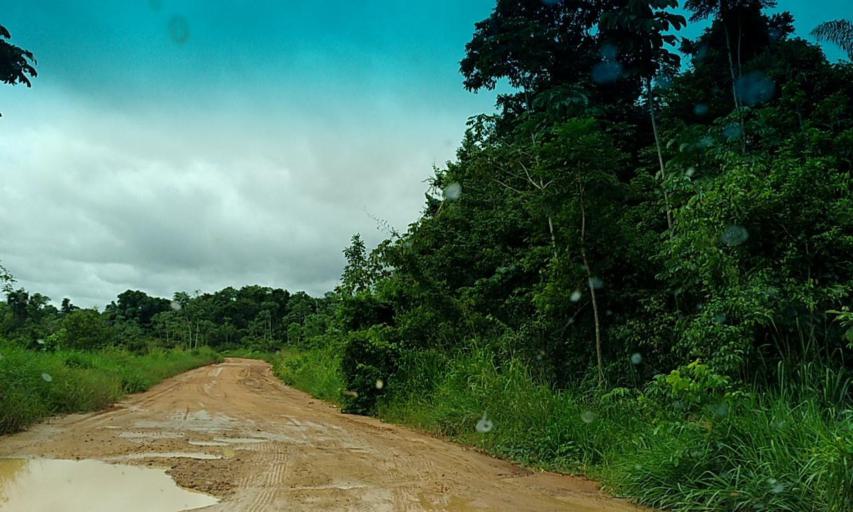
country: BR
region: Para
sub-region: Altamira
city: Altamira
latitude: -3.0851
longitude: -51.6998
